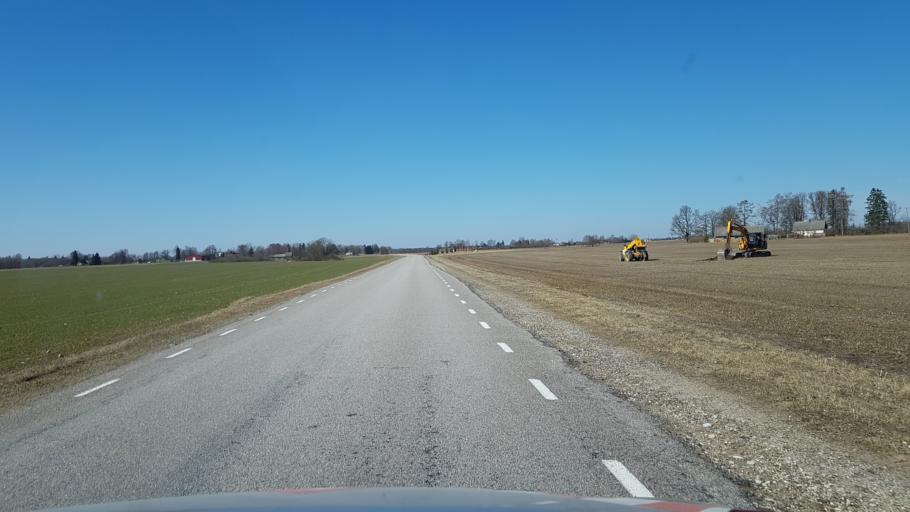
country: EE
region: Laeaene-Virumaa
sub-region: Vaeike-Maarja vald
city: Vaike-Maarja
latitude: 59.1027
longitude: 26.3911
